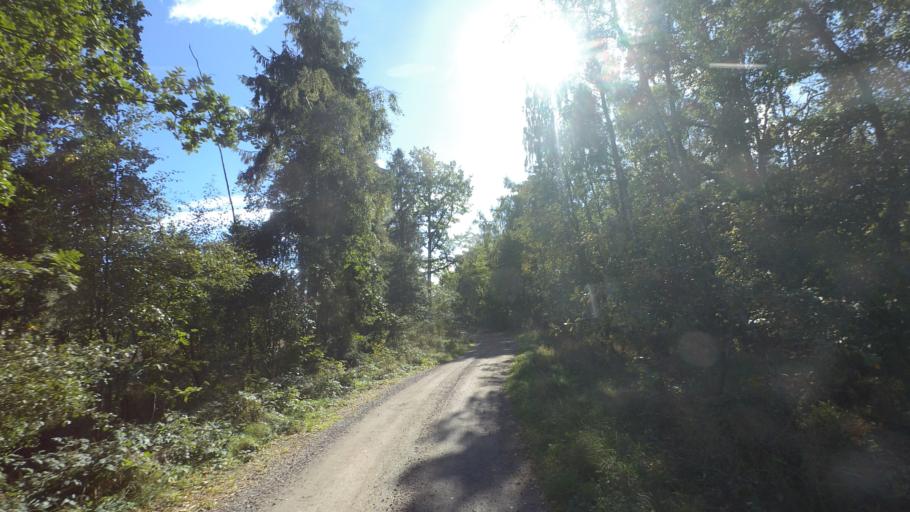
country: DK
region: Capital Region
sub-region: Bornholm Kommune
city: Nexo
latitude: 55.0032
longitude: 15.0880
